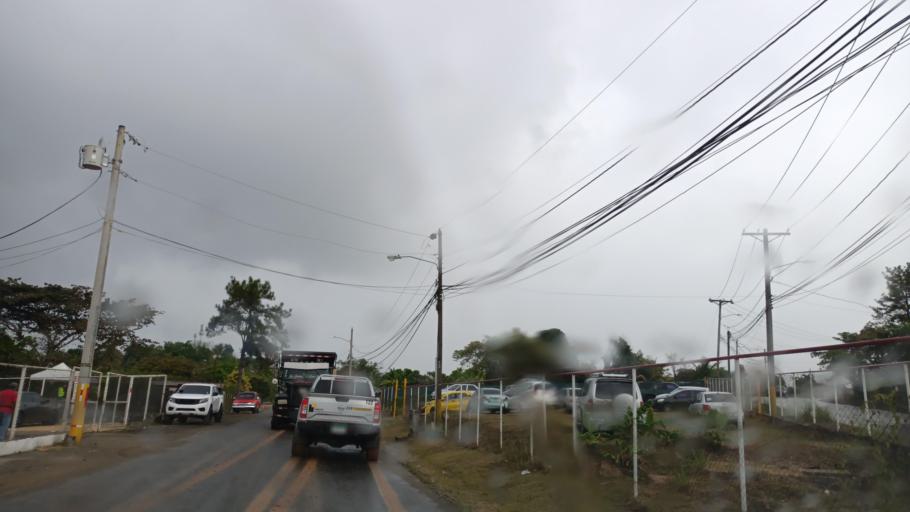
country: PA
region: Panama
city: Caimitillo
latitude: 9.1641
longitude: -79.5492
